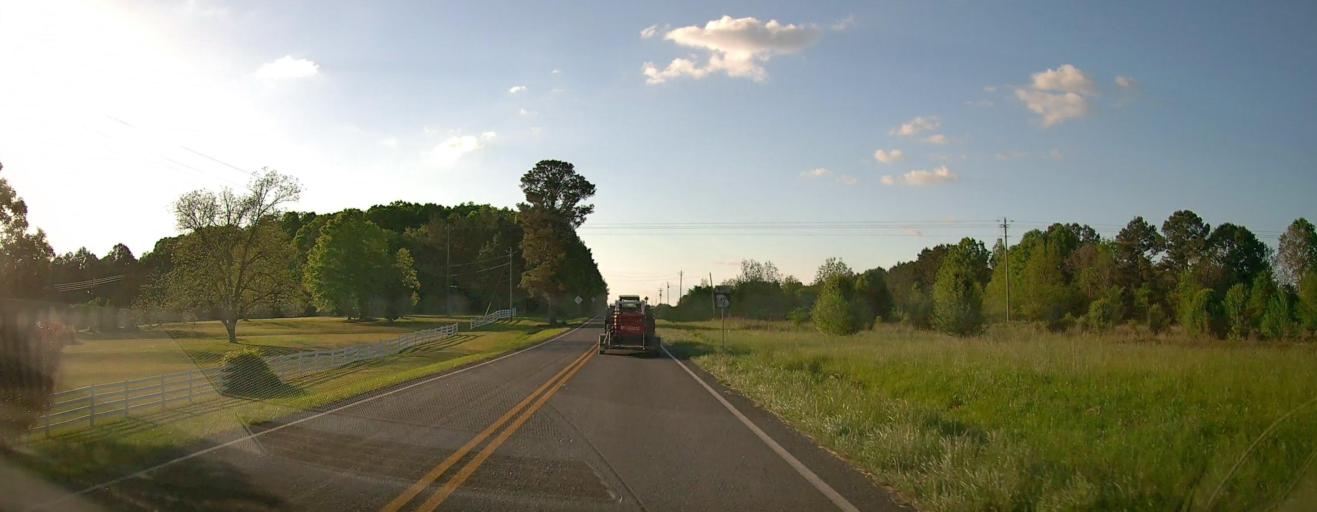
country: US
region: Georgia
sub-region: Jasper County
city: Monticello
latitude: 33.4631
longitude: -83.6345
